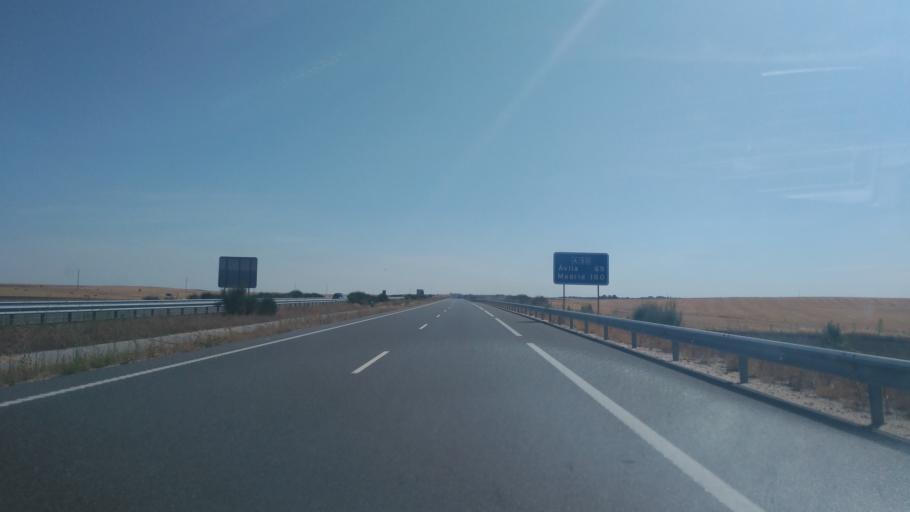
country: ES
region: Castille and Leon
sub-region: Provincia de Salamanca
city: Villar de Gallimazo
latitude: 40.9267
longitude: -5.2923
